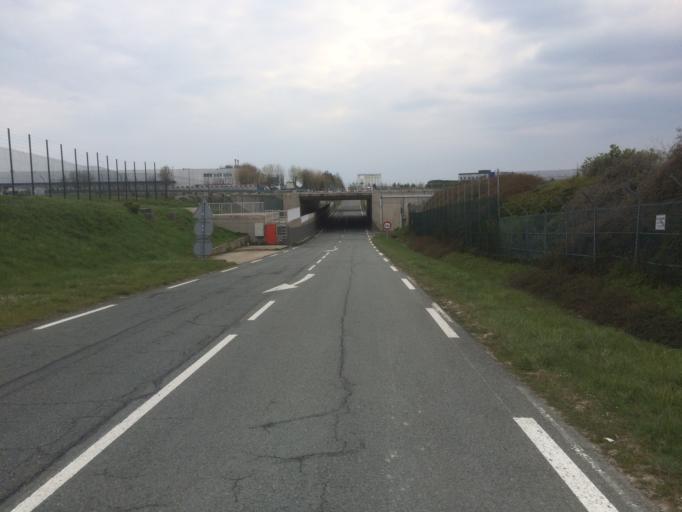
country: FR
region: Ile-de-France
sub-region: Departement de l'Essonne
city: Paray-Vieille-Poste
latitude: 48.7253
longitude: 2.3467
